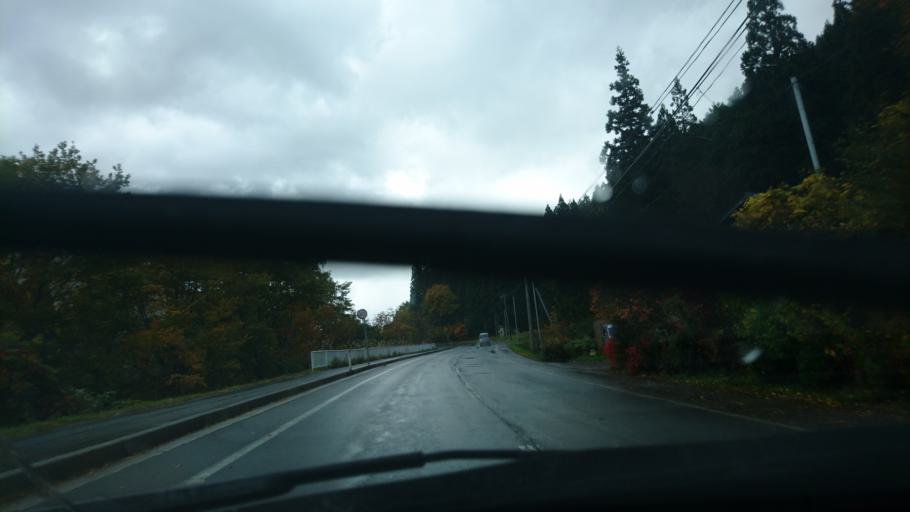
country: JP
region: Iwate
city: Shizukuishi
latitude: 39.5966
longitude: 140.9223
